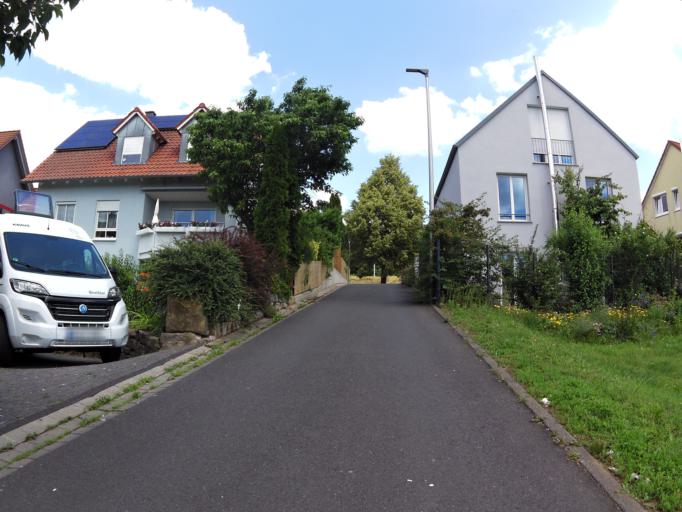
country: DE
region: Bavaria
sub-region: Regierungsbezirk Unterfranken
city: Thungersheim
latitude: 49.8854
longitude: 9.8433
